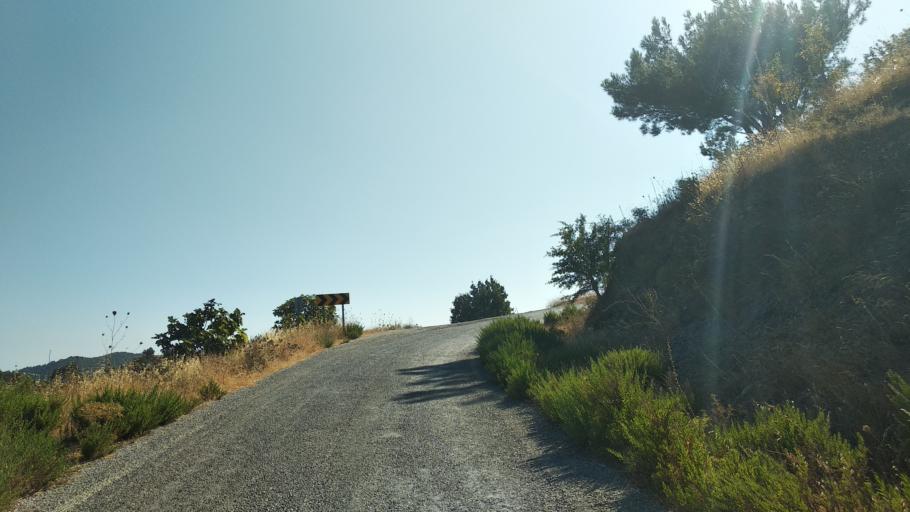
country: TR
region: Izmir
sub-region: Seferihisar
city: Seferhisar
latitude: 38.3251
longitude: 26.9529
